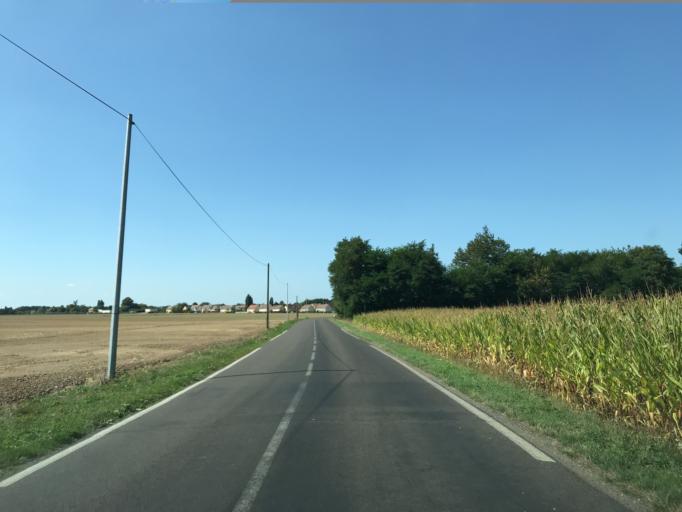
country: FR
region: Haute-Normandie
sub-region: Departement de l'Eure
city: Houlbec-Cocherel
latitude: 49.0950
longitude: 1.3496
